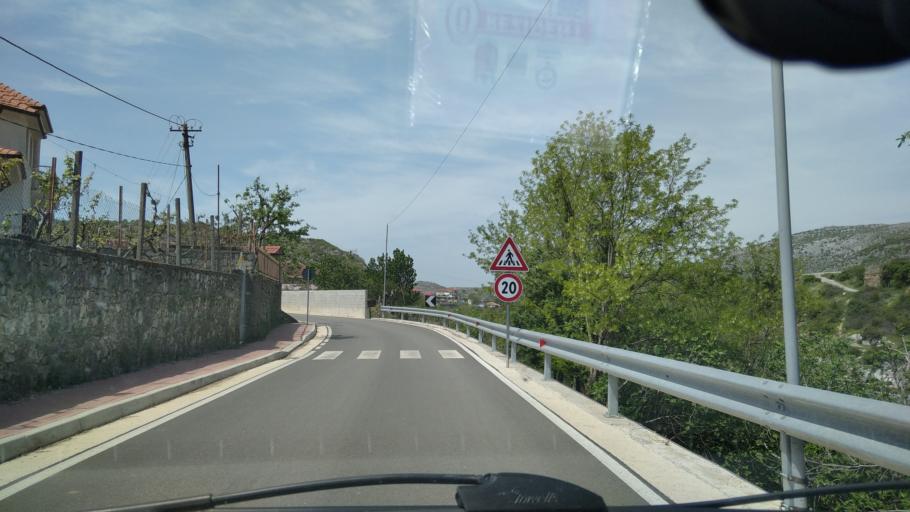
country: AL
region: Shkoder
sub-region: Rrethi i Shkodres
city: Guri i Zi
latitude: 42.1218
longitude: 19.5988
